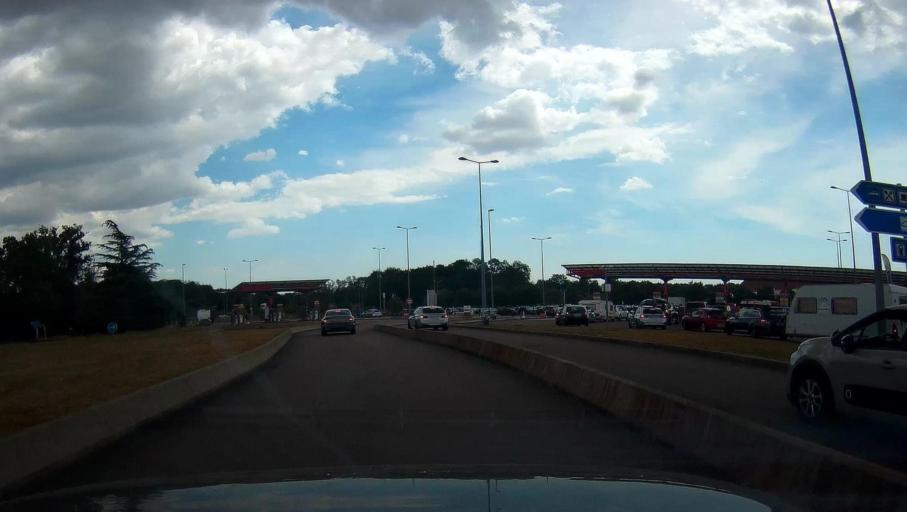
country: FR
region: Bourgogne
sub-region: Departement de la Cote-d'Or
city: Saint-Julien
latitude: 47.4225
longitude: 5.1698
